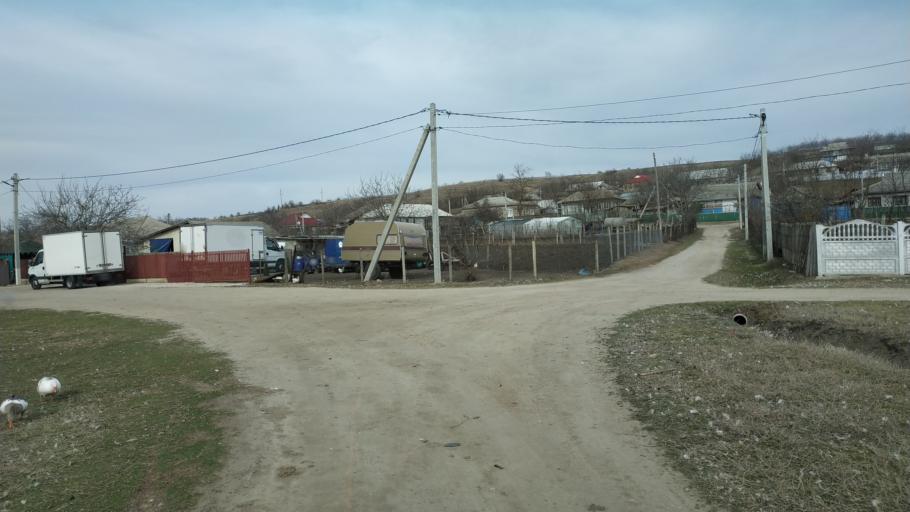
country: RO
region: Vaslui
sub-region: Comuna Dranceni
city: Dranceni
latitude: 46.8755
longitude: 28.2029
